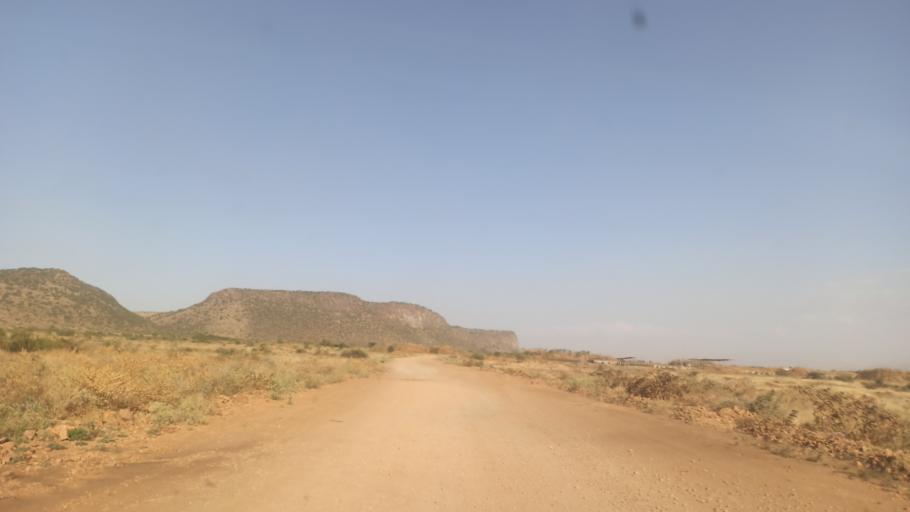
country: ET
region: Oromiya
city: Ziway
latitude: 7.9354
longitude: 38.6168
